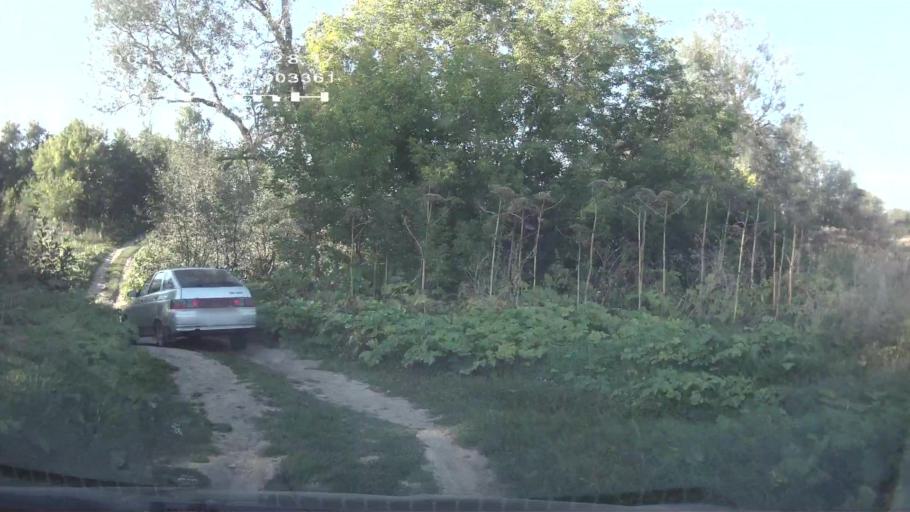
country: RU
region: Mariy-El
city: Morki
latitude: 56.3591
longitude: 48.9033
